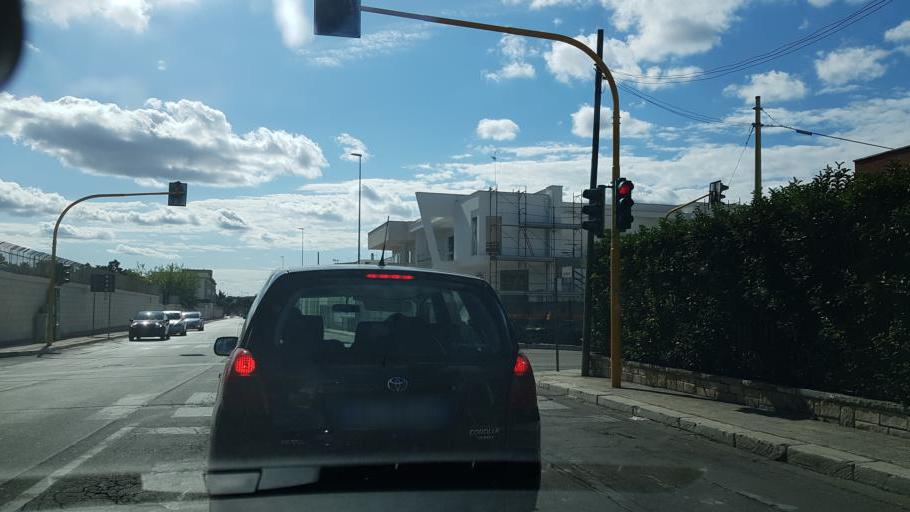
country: IT
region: Apulia
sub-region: Provincia di Lecce
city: Lecce
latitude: 40.3504
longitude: 18.1518
